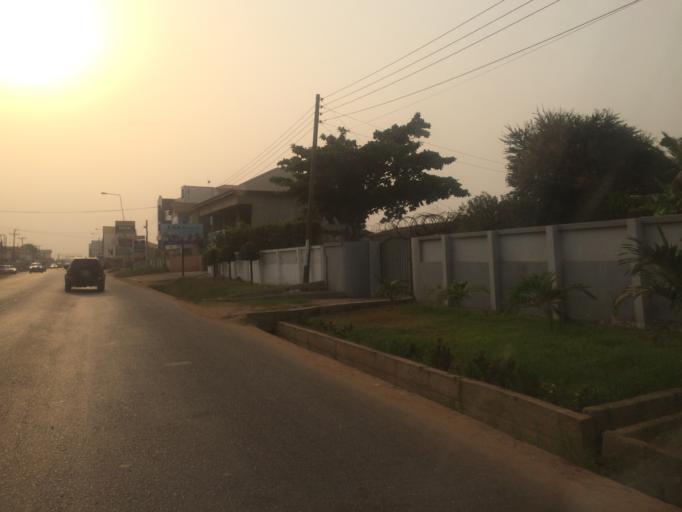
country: GH
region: Greater Accra
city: Nungua
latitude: 5.6359
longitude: -0.1023
